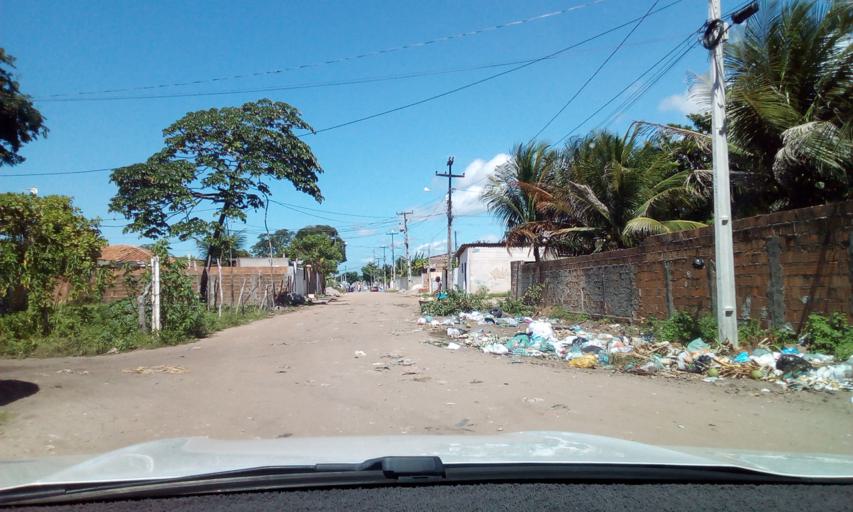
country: BR
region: Paraiba
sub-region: Joao Pessoa
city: Joao Pessoa
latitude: -7.1761
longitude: -34.8150
